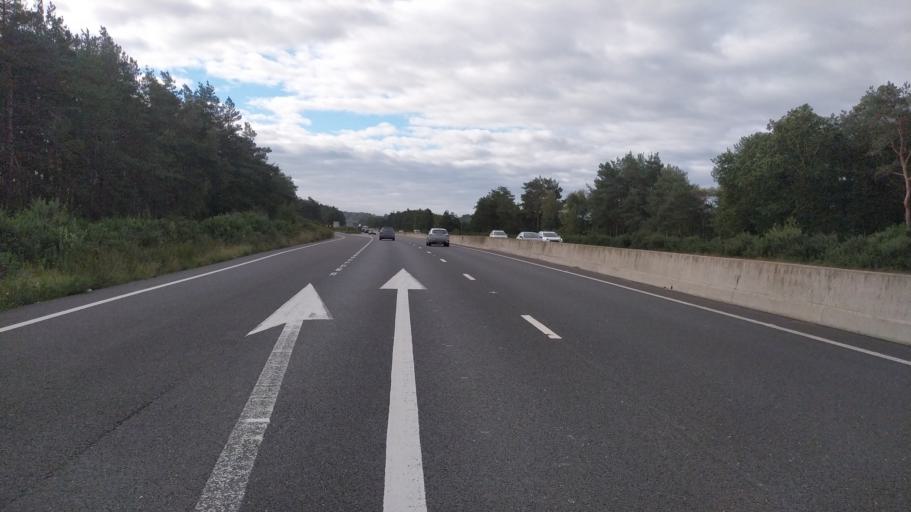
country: GB
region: England
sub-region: Dorset
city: Christchurch
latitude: 50.7861
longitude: -1.8135
